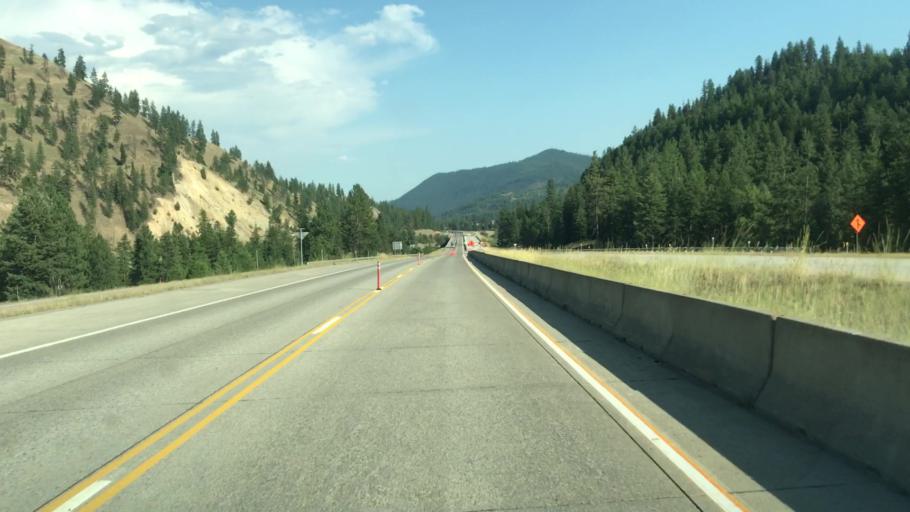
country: US
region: Montana
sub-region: Mineral County
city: Superior
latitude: 47.2248
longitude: -114.9670
